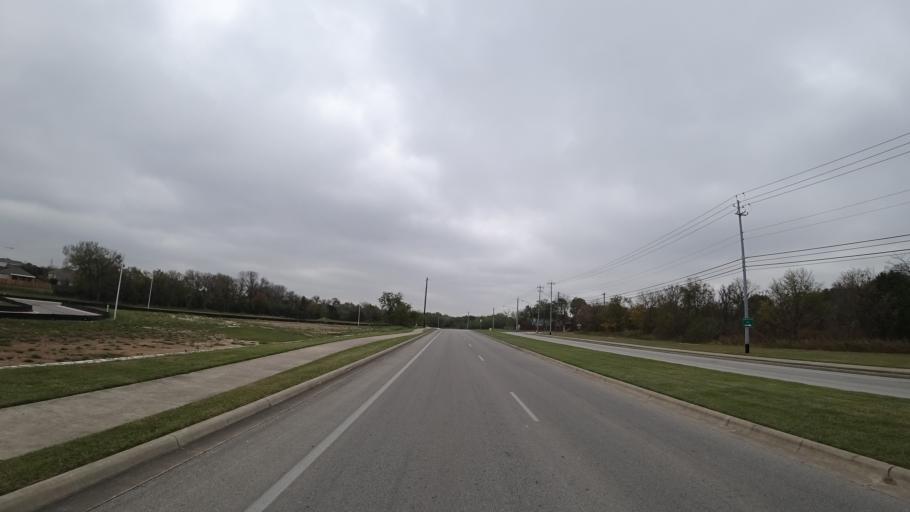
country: US
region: Texas
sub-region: Travis County
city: Pflugerville
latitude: 30.3724
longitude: -97.6556
